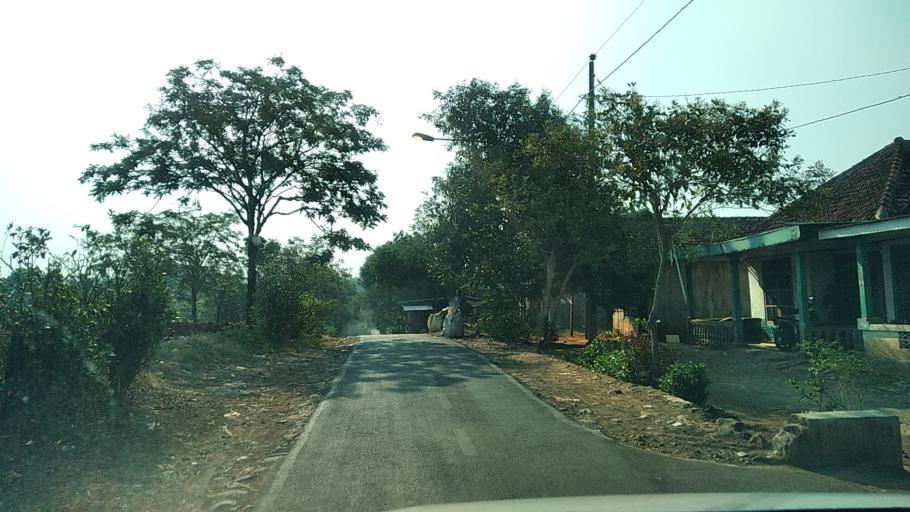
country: ID
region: Central Java
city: Semarang
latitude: -7.0232
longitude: 110.3012
